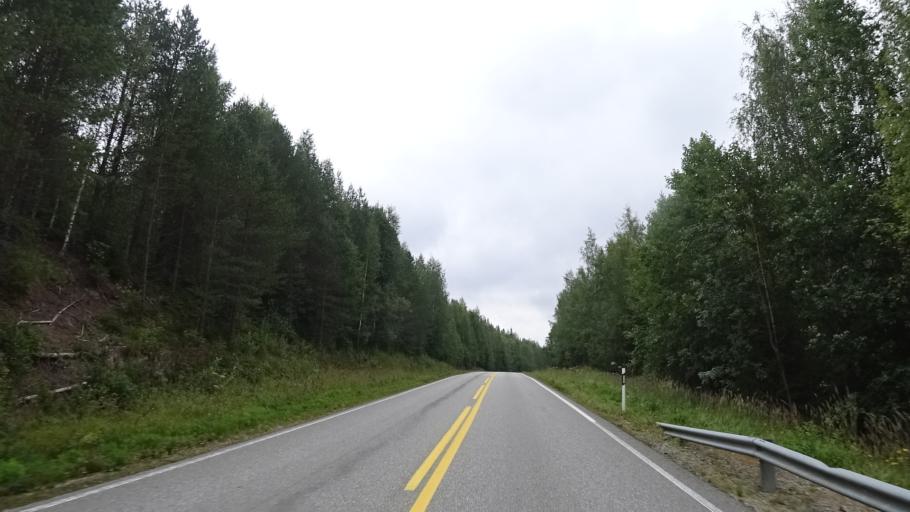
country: FI
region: North Karelia
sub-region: Pielisen Karjala
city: Lieksa
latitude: 63.2806
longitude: 30.5809
